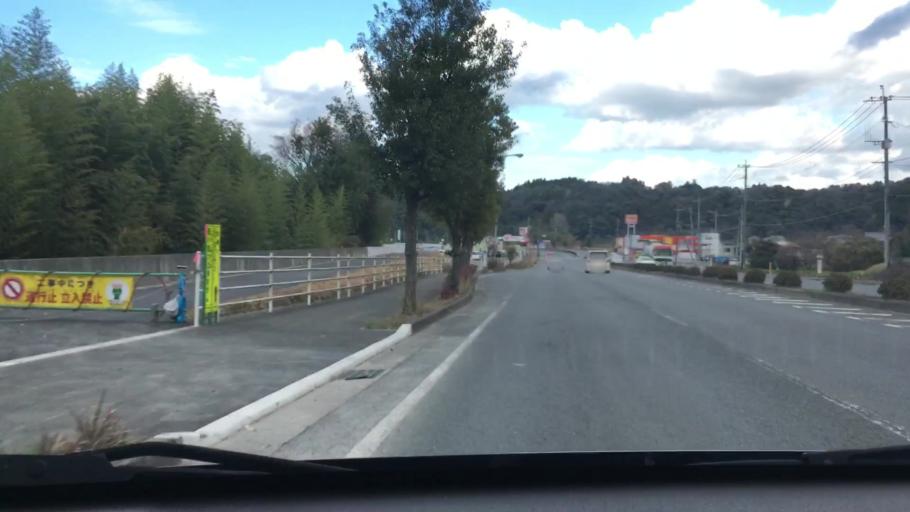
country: JP
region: Oita
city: Oita
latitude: 33.1299
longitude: 131.6581
